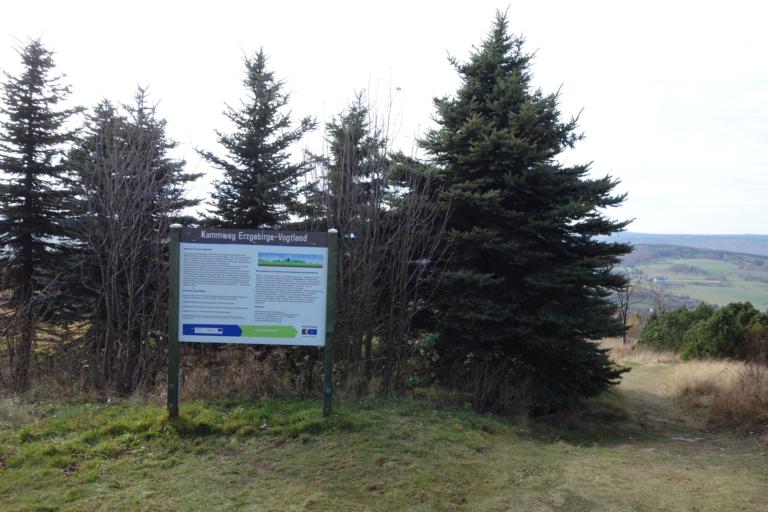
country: DE
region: Saxony
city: Neuhausen
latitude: 50.6589
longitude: 13.4655
